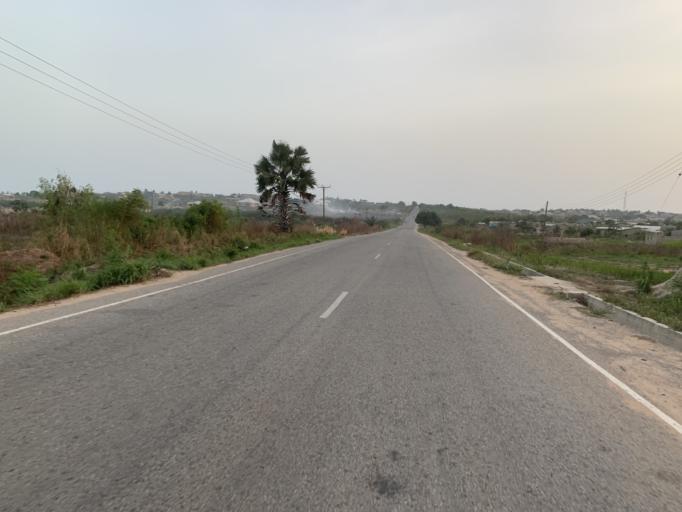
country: GH
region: Central
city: Winneba
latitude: 5.3669
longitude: -0.6081
